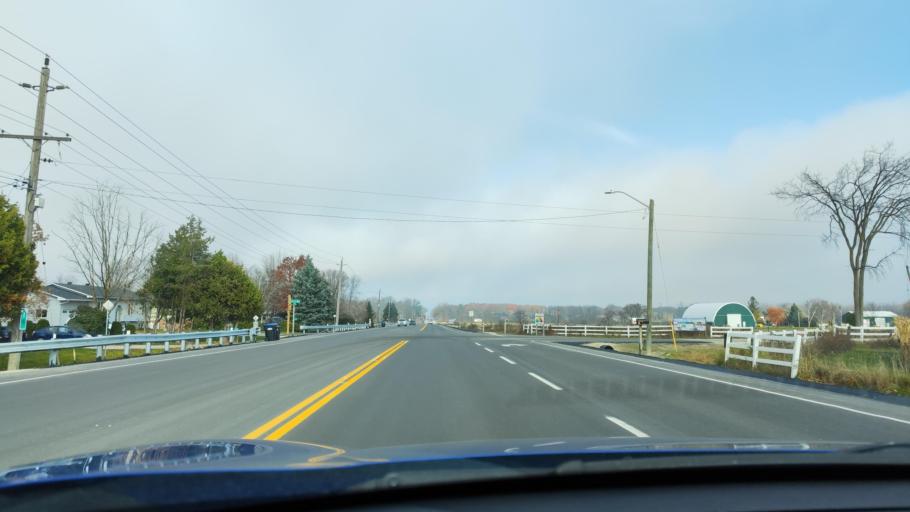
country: CA
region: Ontario
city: Wasaga Beach
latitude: 44.4560
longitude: -80.0715
